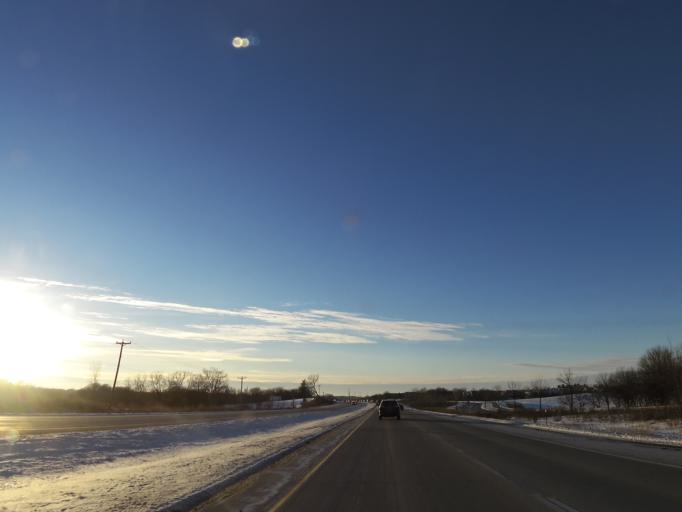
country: US
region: Minnesota
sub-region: Carver County
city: Chanhassen
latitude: 44.8633
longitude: -93.5640
